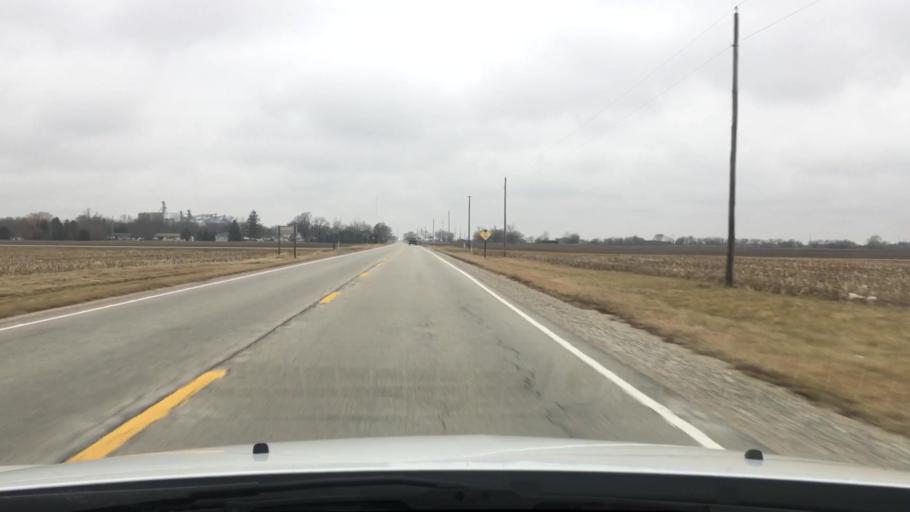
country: US
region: Illinois
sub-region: Iroquois County
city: Clifton
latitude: 40.8851
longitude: -87.9405
